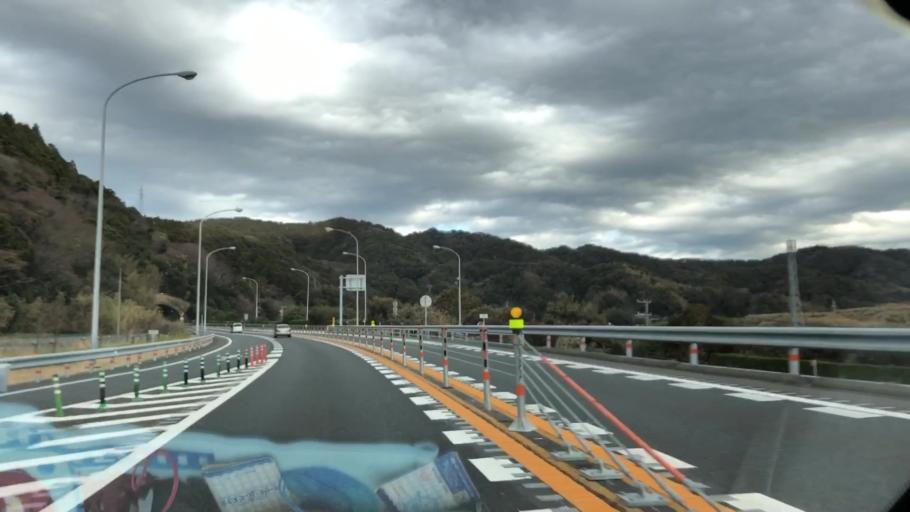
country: JP
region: Chiba
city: Tateyama
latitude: 35.1152
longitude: 139.8515
